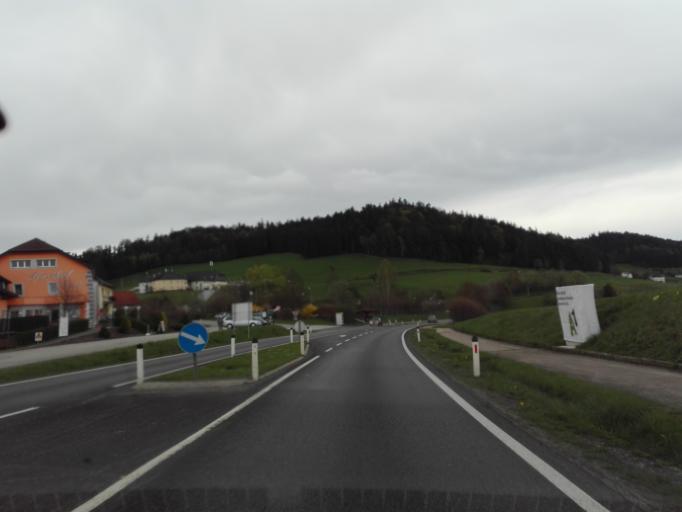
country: AT
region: Upper Austria
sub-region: Politischer Bezirk Rohrbach
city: Schlaegl
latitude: 48.5999
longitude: 13.9579
